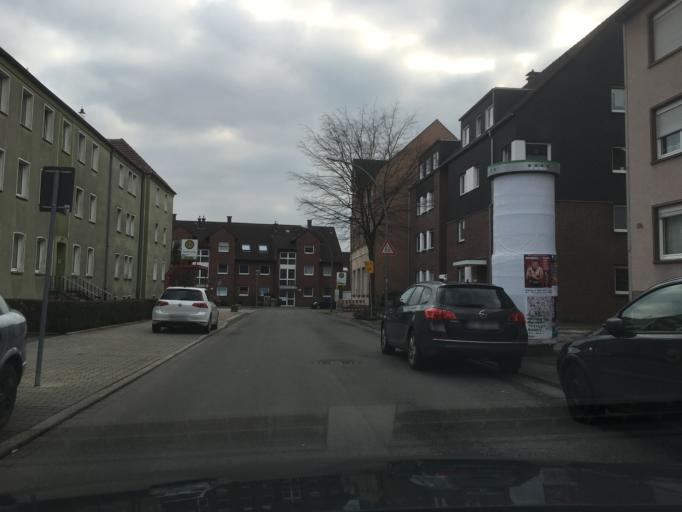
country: DE
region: North Rhine-Westphalia
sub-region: Regierungsbezirk Munster
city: Gladbeck
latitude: 51.5597
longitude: 6.9943
